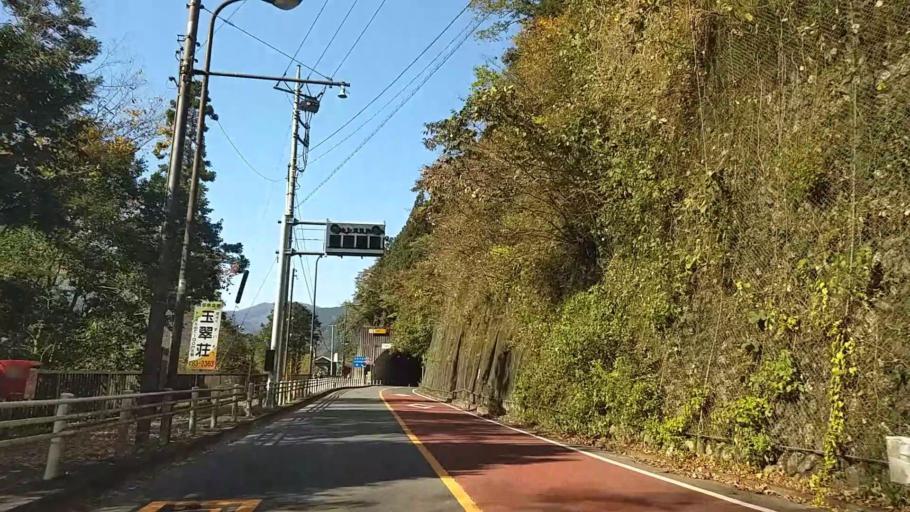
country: JP
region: Tokyo
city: Itsukaichi
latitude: 35.8031
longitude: 139.1038
